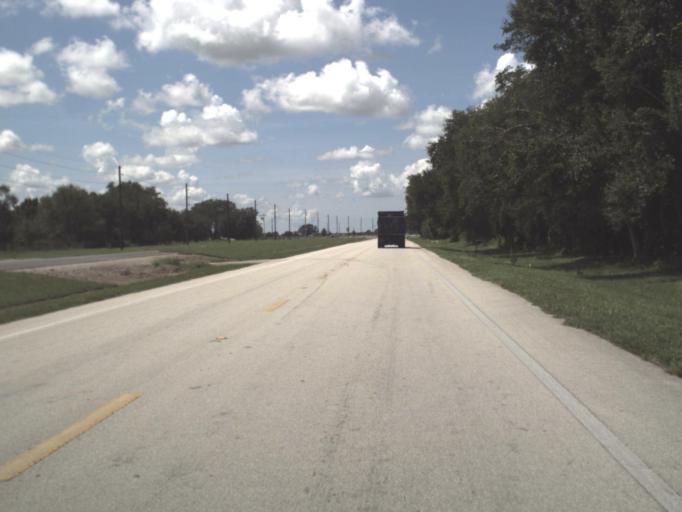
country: US
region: Florida
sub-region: DeSoto County
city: Nocatee
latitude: 27.1365
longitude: -81.9000
